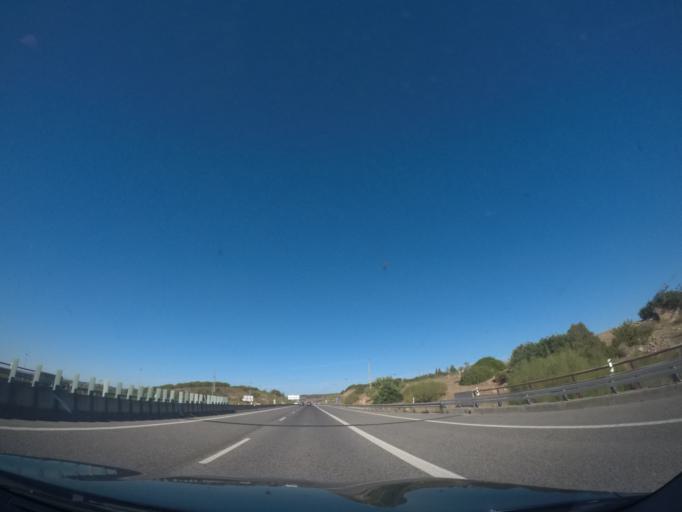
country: PT
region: Faro
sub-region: Portimao
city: Alvor
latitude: 37.1728
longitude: -8.6339
